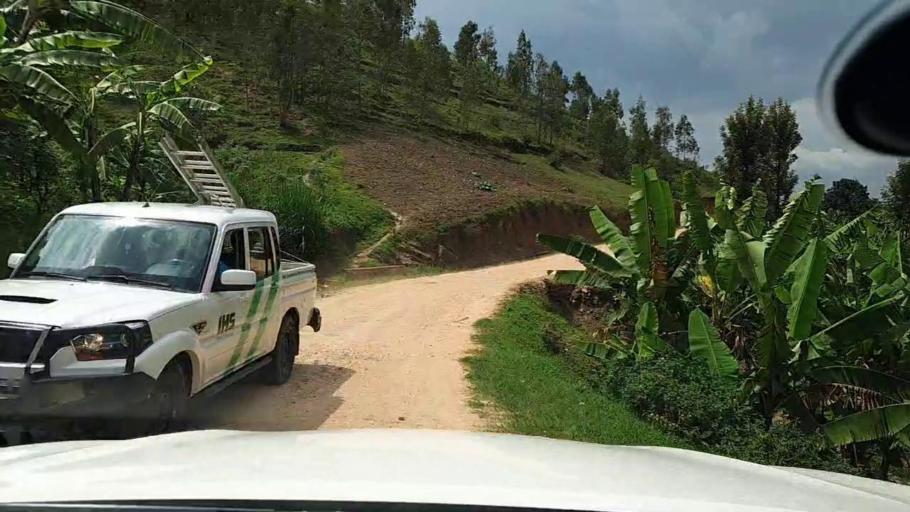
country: RW
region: Western Province
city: Kibuye
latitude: -2.1176
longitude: 29.4237
